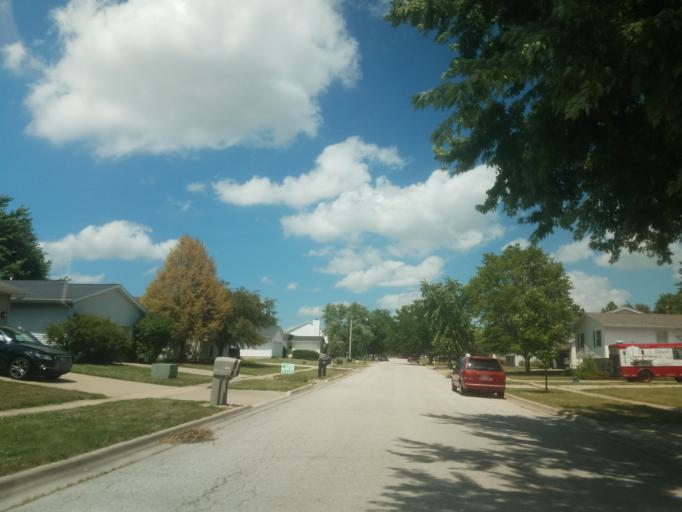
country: US
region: Illinois
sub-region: McLean County
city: Bloomington
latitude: 40.4433
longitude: -89.0303
